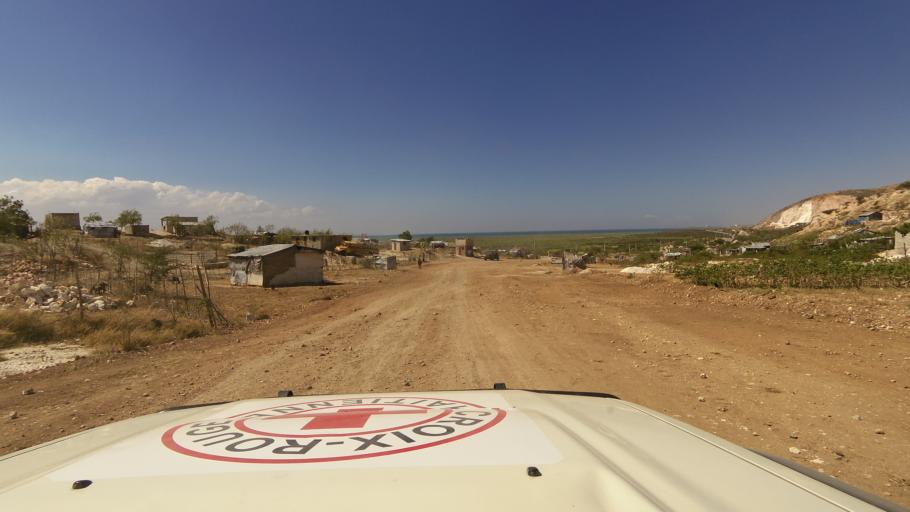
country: HT
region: Ouest
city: Croix des Bouquets
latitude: 18.6668
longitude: -72.2961
